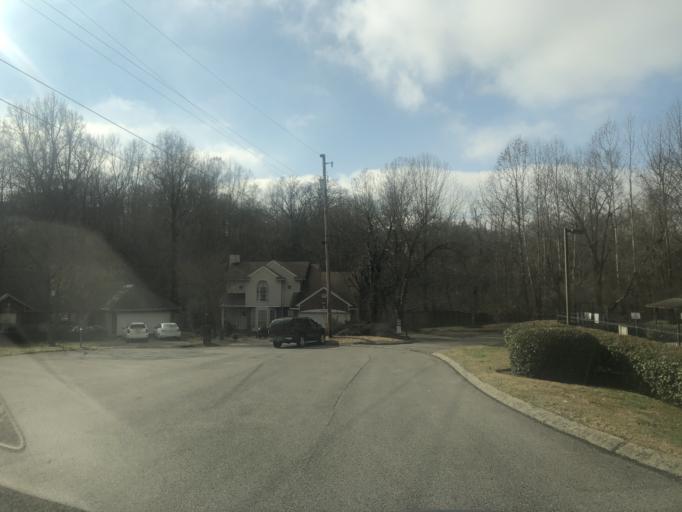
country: US
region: Tennessee
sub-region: Rutherford County
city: La Vergne
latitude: 36.0770
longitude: -86.6564
